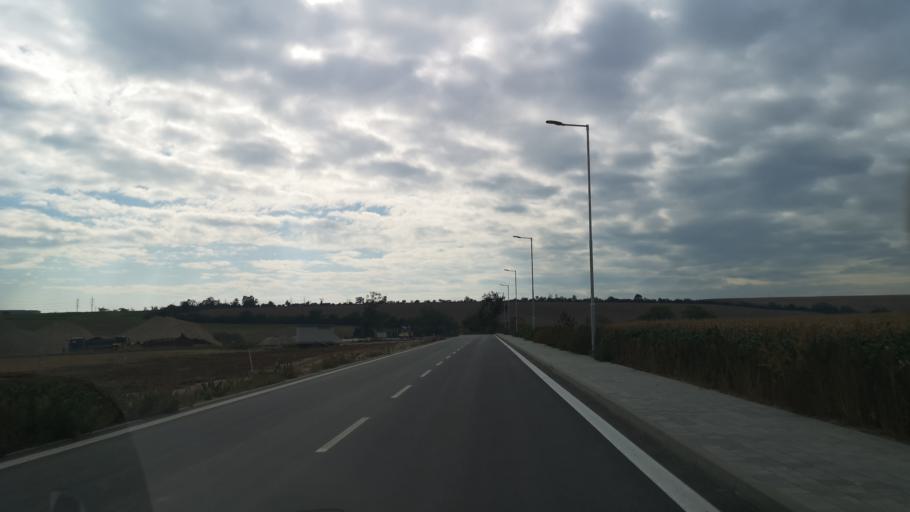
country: SK
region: Nitriansky
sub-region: Okres Nitra
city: Nitra
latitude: 48.3239
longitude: 18.0231
